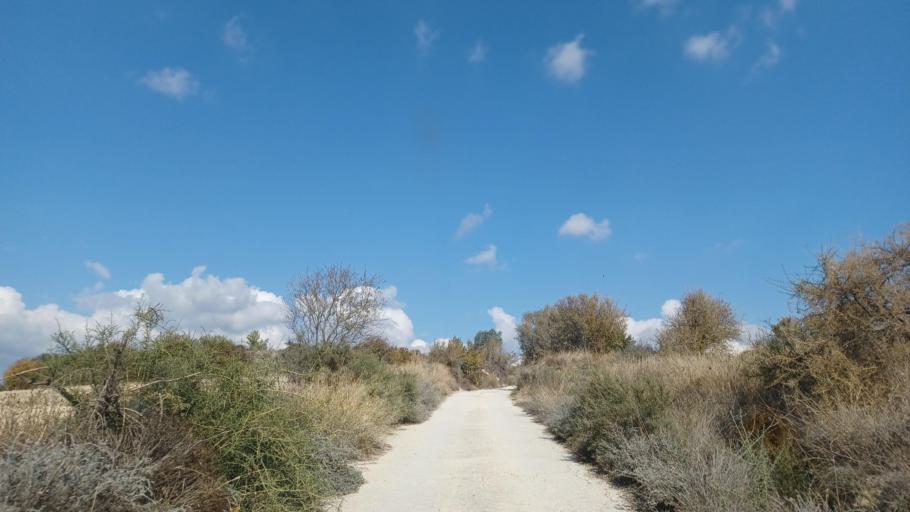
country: CY
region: Pafos
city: Mesogi
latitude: 34.8396
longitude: 32.5693
